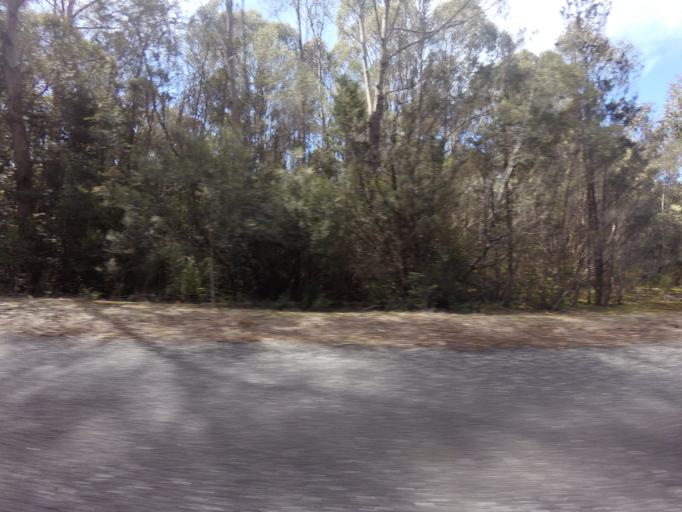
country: AU
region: Tasmania
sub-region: West Coast
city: Queenstown
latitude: -42.8022
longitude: 146.0958
